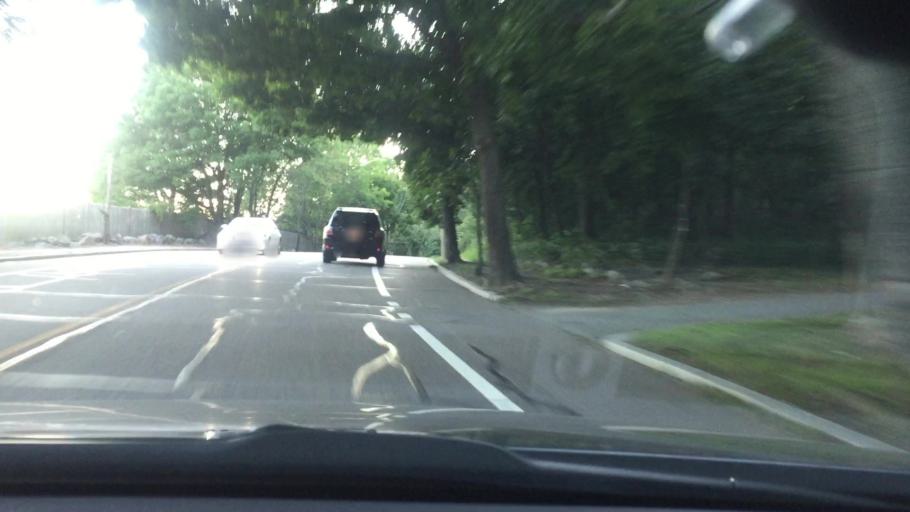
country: US
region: Massachusetts
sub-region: Middlesex County
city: Newton
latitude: 42.3000
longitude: -71.1924
